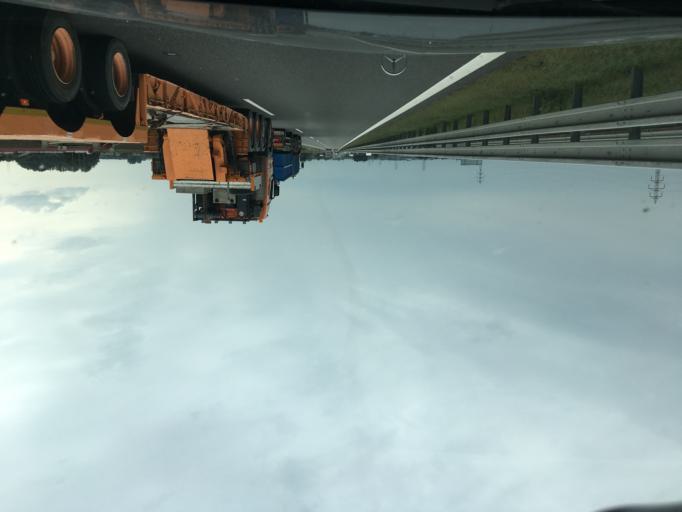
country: CZ
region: South Moravian
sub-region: Okres Breclav
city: Moravsky Zizkov
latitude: 48.8042
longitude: 16.9001
